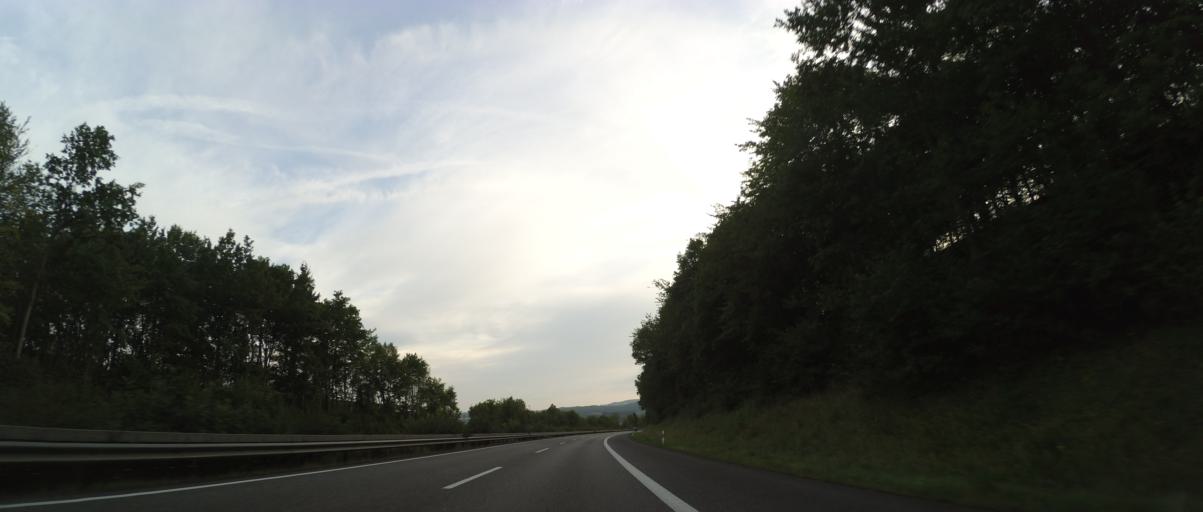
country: DE
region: Rheinland-Pfalz
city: Brockscheid
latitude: 50.1361
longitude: 6.8618
